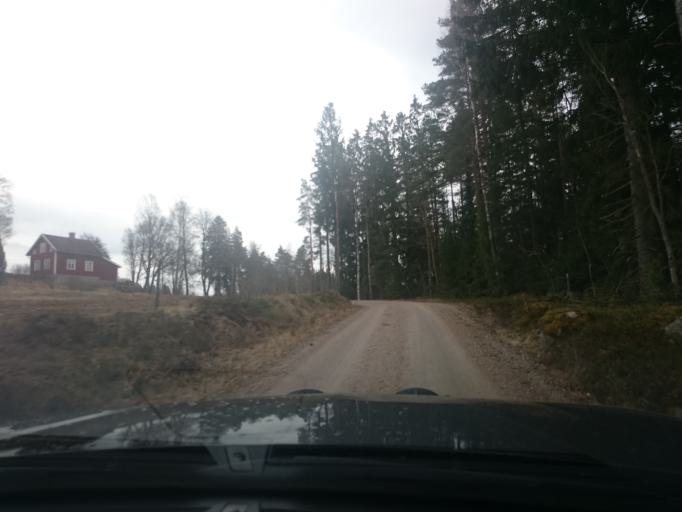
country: SE
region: Joenkoeping
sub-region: Vetlanda Kommun
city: Vetlanda
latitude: 57.2793
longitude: 15.1781
